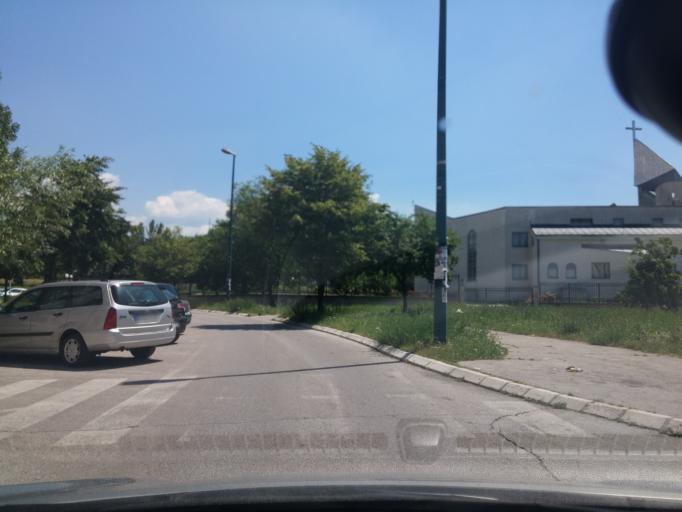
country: BA
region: Federation of Bosnia and Herzegovina
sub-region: Kanton Sarajevo
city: Sarajevo
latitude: 43.8415
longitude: 18.3495
